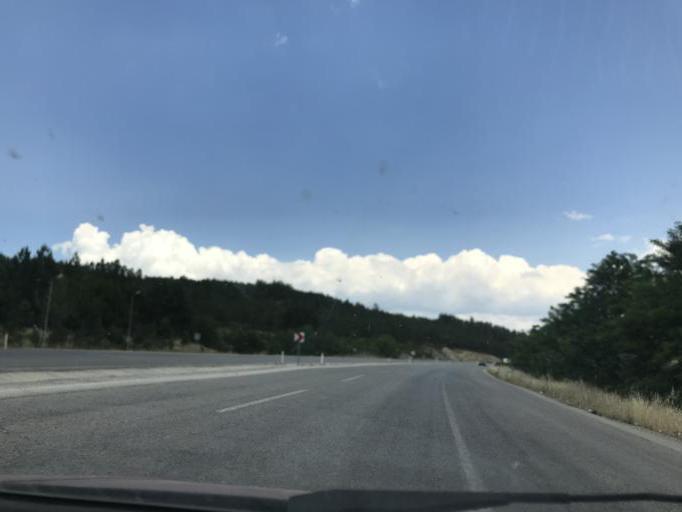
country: TR
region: Denizli
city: Tavas
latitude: 37.6140
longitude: 29.1445
